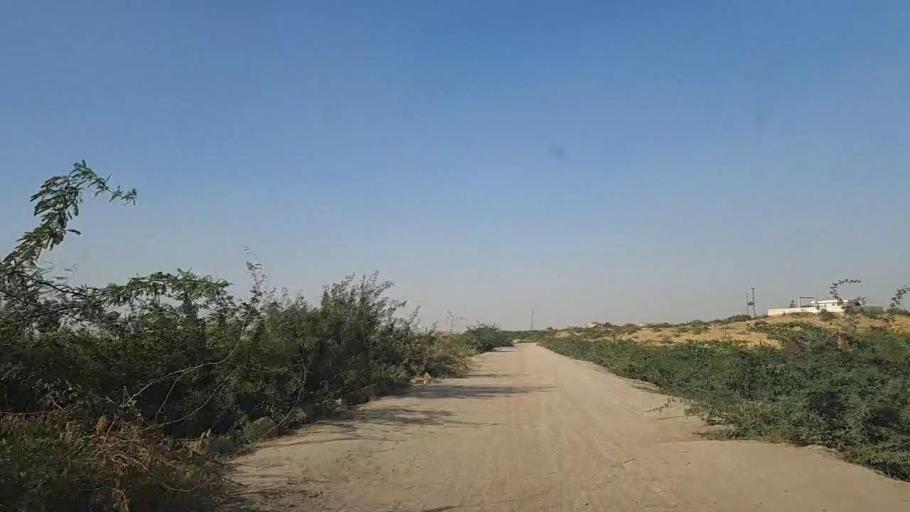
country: PK
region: Sindh
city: Daro Mehar
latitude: 25.0460
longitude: 68.1356
